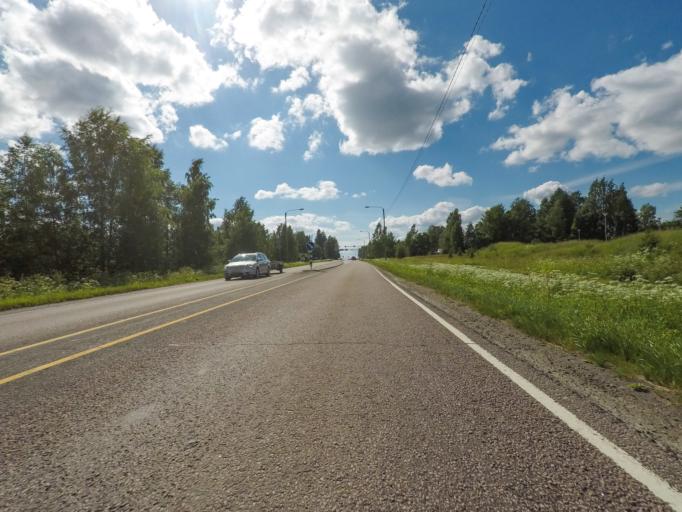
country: FI
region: Southern Savonia
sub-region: Savonlinna
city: Kerimaeki
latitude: 61.8840
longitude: 29.0926
